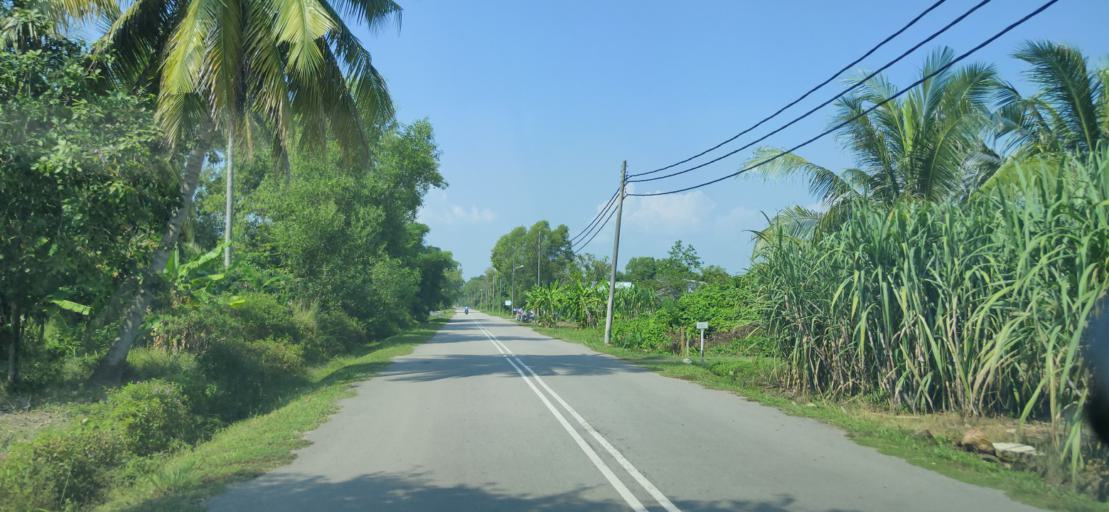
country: MY
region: Kedah
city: Sungai Petani
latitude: 5.6742
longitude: 100.4623
